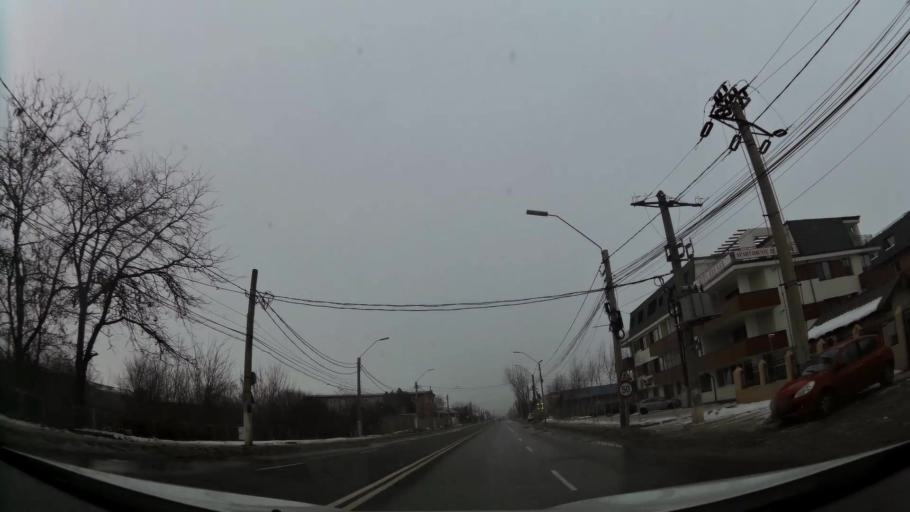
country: RO
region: Ilfov
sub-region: Comuna Magurele
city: Magurele
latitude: 44.3623
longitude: 26.0384
